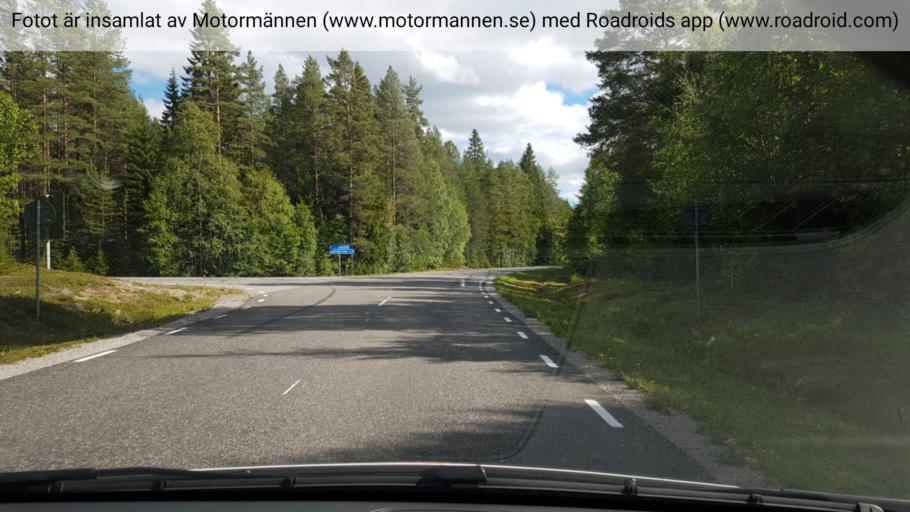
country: SE
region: Vaesterbotten
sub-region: Umea Kommun
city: Hoernefors
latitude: 63.6798
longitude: 19.9135
